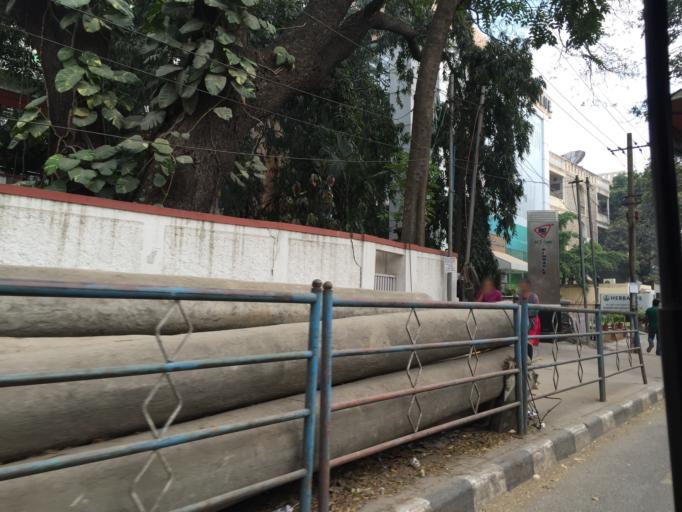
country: IN
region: Karnataka
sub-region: Bangalore Urban
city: Bangalore
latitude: 12.9715
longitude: 77.6105
